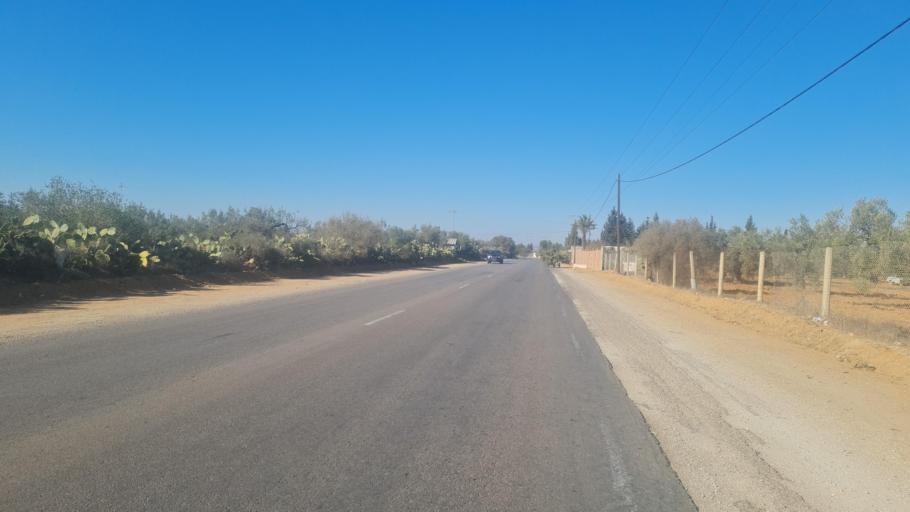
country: TN
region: Susah
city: Sidi Bou Ali
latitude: 35.9085
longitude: 10.3830
